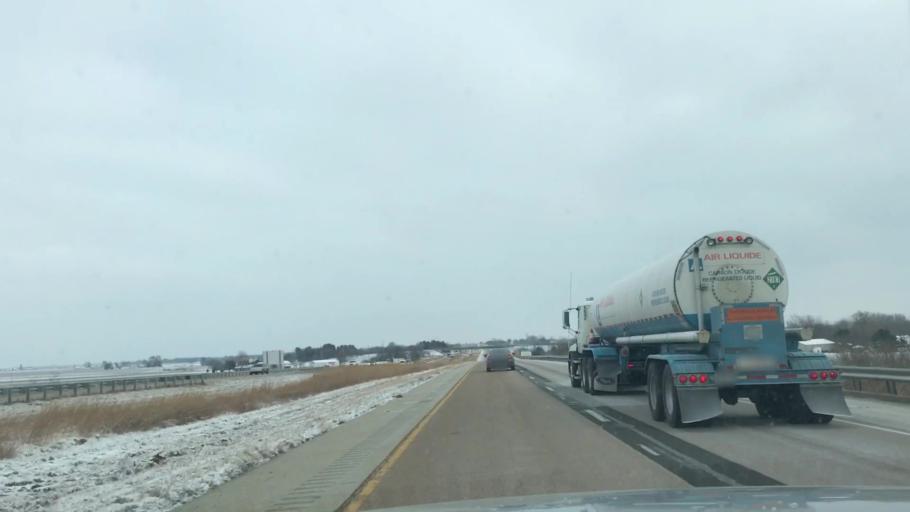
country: US
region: Illinois
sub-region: Montgomery County
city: Litchfield
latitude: 39.1984
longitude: -89.6643
